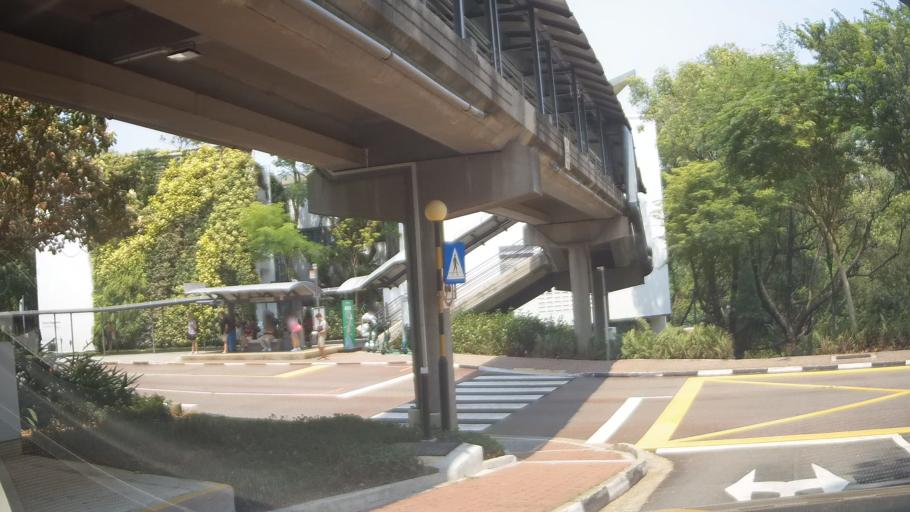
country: SG
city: Singapore
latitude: 1.2954
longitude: 103.7709
